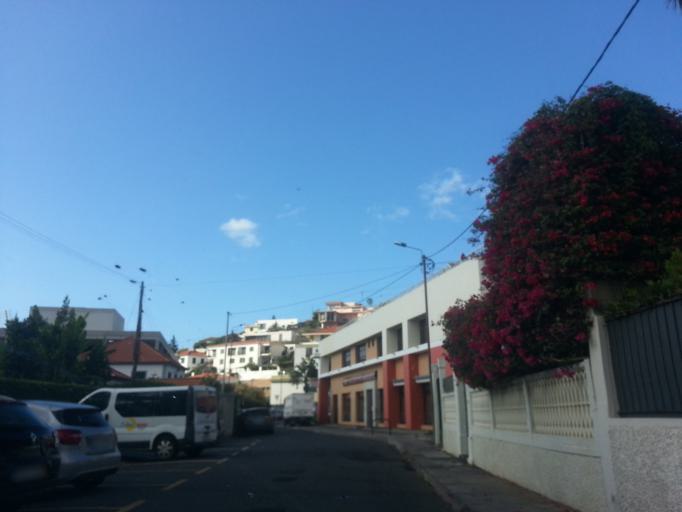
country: PT
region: Madeira
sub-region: Funchal
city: Funchal
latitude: 32.6468
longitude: -16.9296
